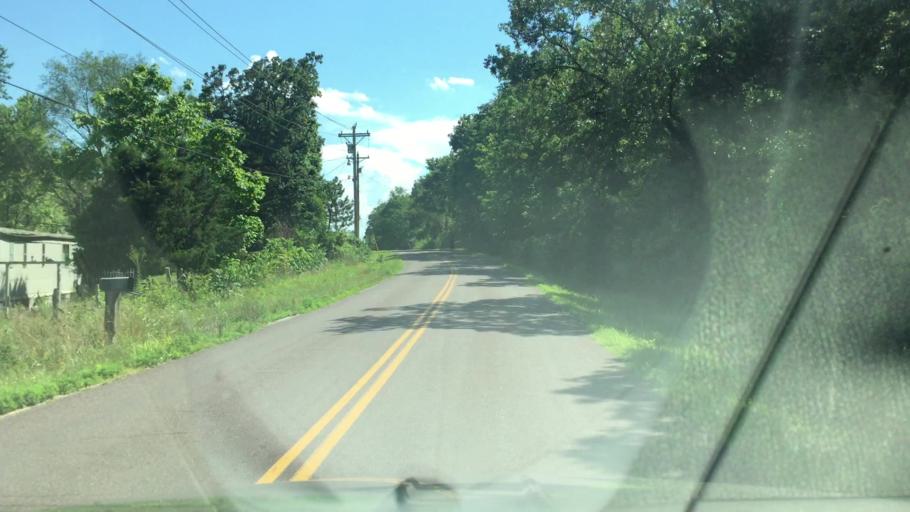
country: US
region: Missouri
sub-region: Miller County
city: Tuscumbia
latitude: 38.0912
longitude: -92.4819
